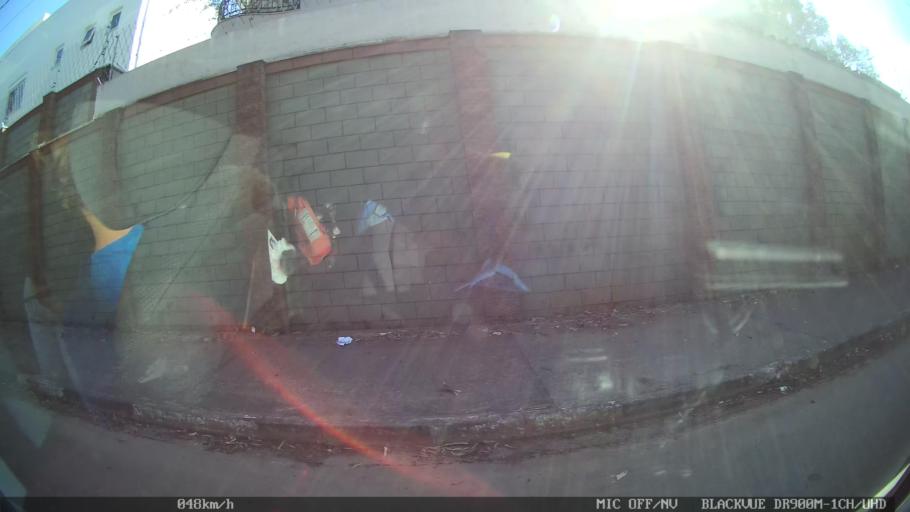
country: BR
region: Sao Paulo
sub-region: Sumare
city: Sumare
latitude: -22.8206
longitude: -47.2810
